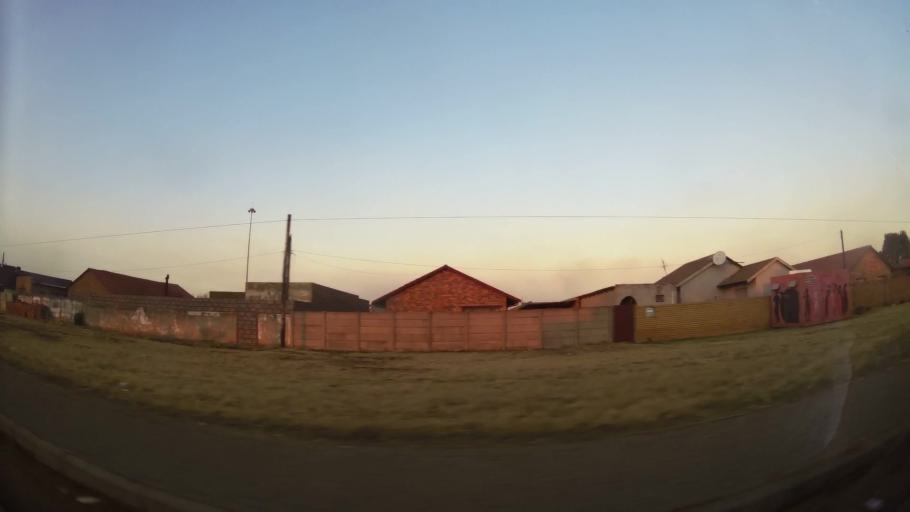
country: ZA
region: Gauteng
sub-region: Ekurhuleni Metropolitan Municipality
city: Springs
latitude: -26.2996
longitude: 28.4073
